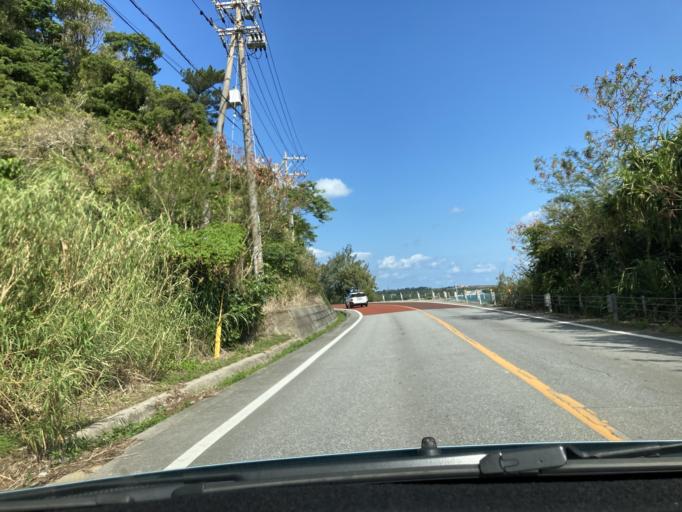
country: JP
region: Okinawa
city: Nago
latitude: 26.6368
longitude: 128.0036
